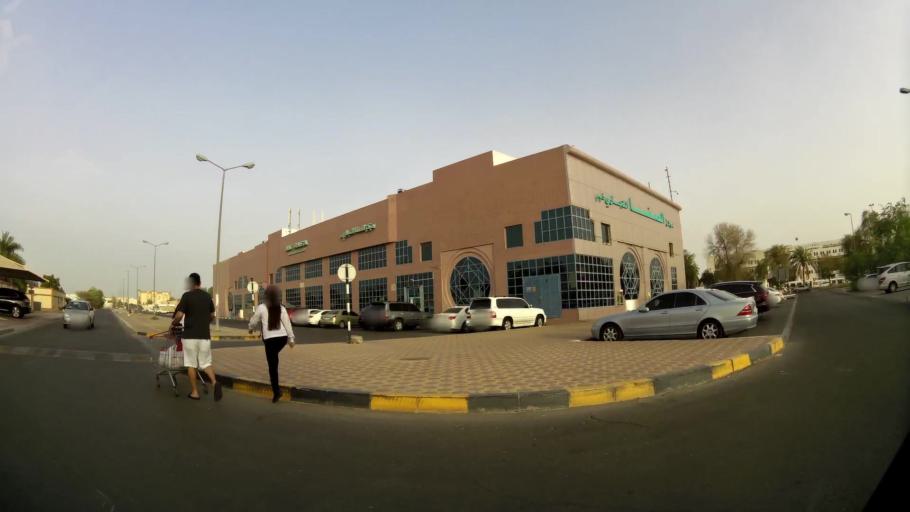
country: AE
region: Abu Dhabi
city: Al Ain
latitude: 24.2428
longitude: 55.7300
